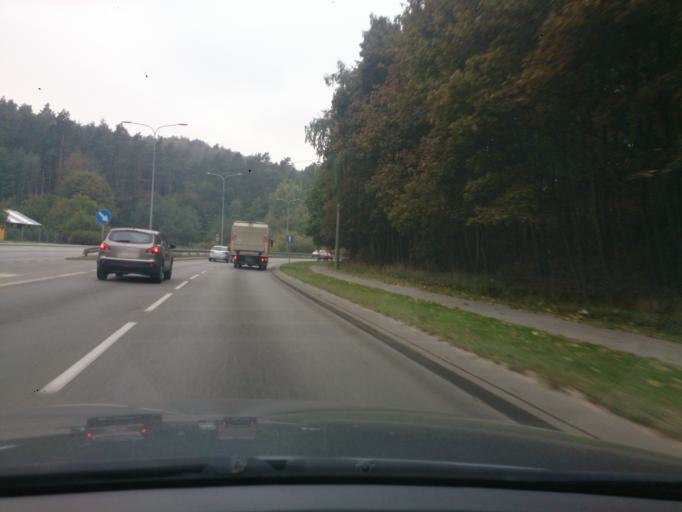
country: PL
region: Pomeranian Voivodeship
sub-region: Powiat gdanski
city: Kowale
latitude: 54.3707
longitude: 18.5604
